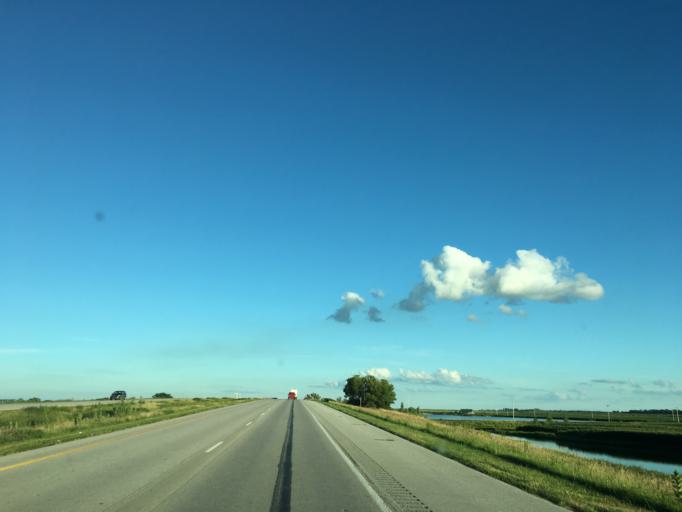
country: US
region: Nebraska
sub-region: Otoe County
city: Nebraska City
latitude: 40.6718
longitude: -95.7683
